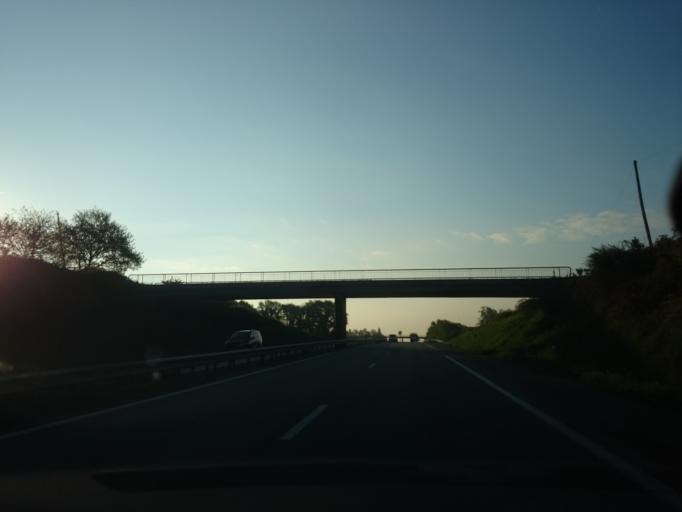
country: FR
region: Brittany
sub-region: Departement du Finistere
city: Chateaulin
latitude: 48.2191
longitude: -4.0609
